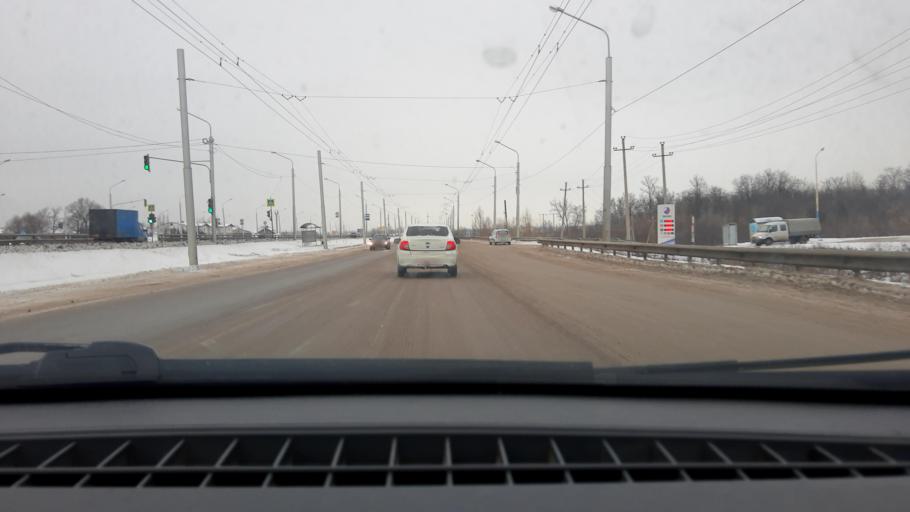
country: RU
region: Bashkortostan
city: Ufa
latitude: 54.7696
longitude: 55.9565
